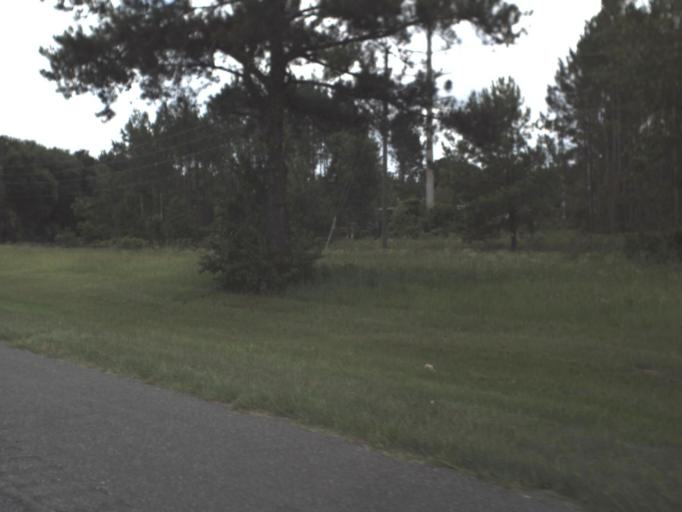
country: US
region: Florida
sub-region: Columbia County
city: Five Points
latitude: 30.2197
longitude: -82.7105
